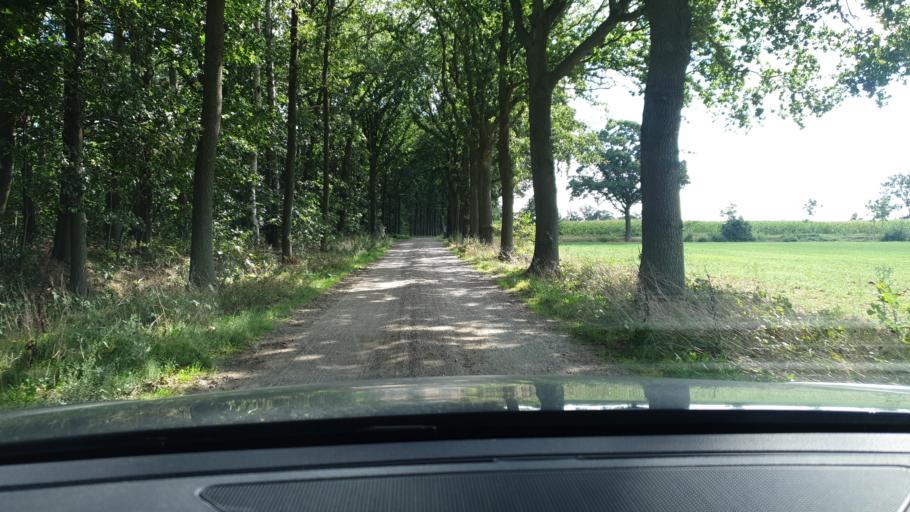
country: NL
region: North Brabant
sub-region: Gemeente Veghel
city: Eerde
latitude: 51.5864
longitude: 5.5110
